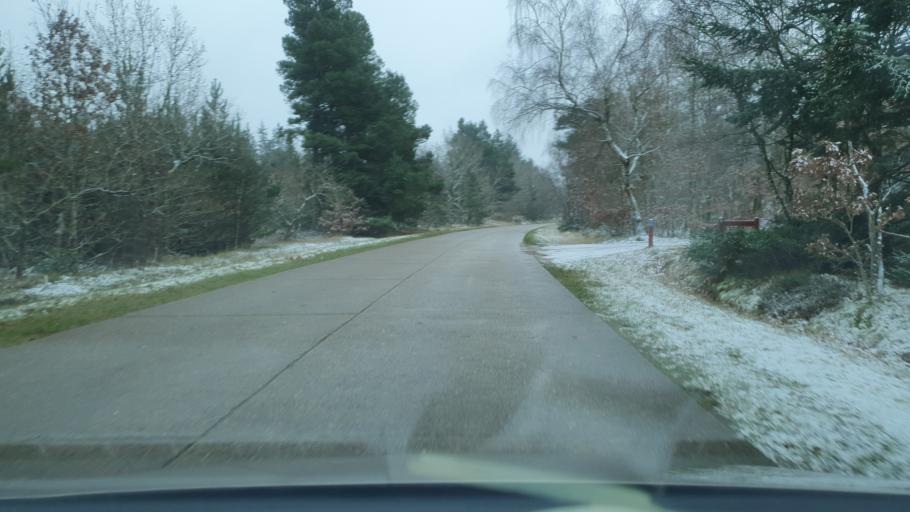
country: DK
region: North Denmark
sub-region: Jammerbugt Kommune
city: Brovst
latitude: 57.1391
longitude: 9.4607
